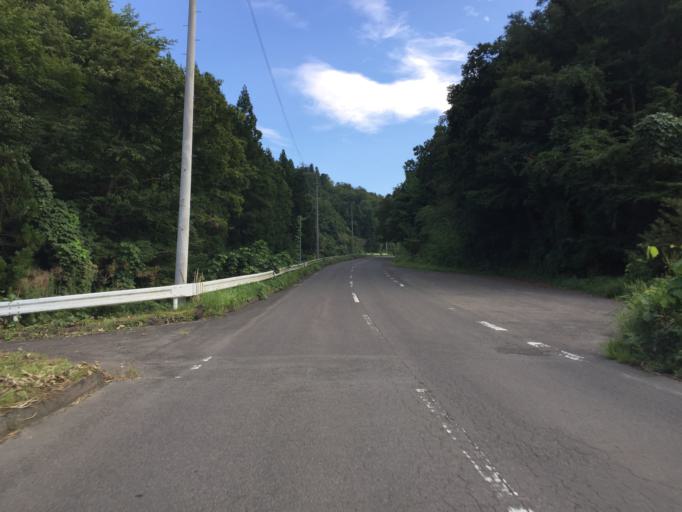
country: JP
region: Fukushima
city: Fukushima-shi
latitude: 37.6617
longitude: 140.5719
